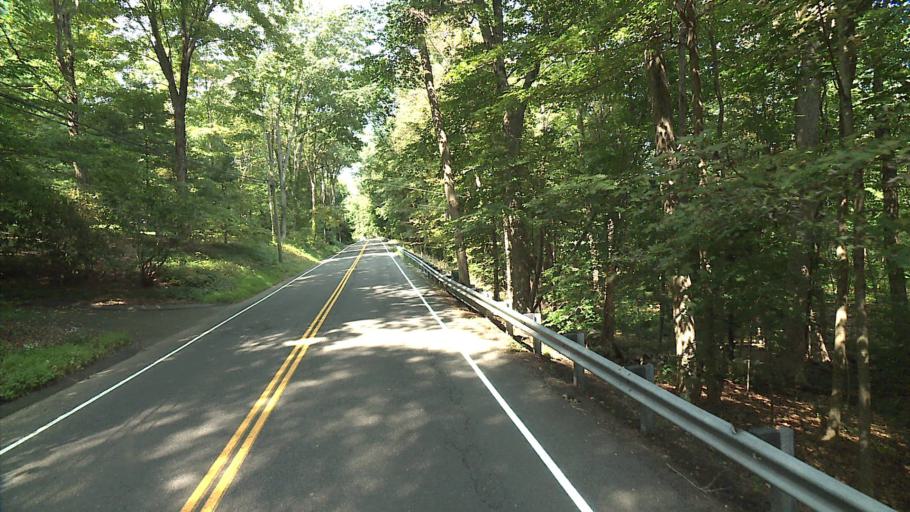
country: US
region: Connecticut
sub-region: Fairfield County
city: Bethel
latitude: 41.3351
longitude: -73.3771
